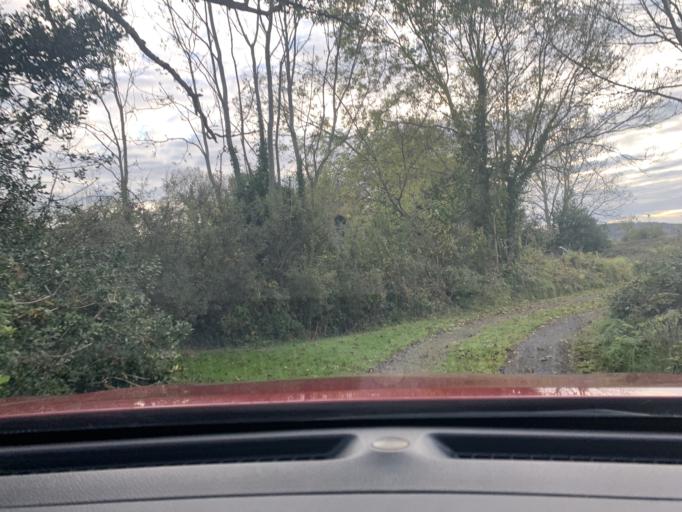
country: IE
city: Ballisodare
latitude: 54.2311
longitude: -8.5065
